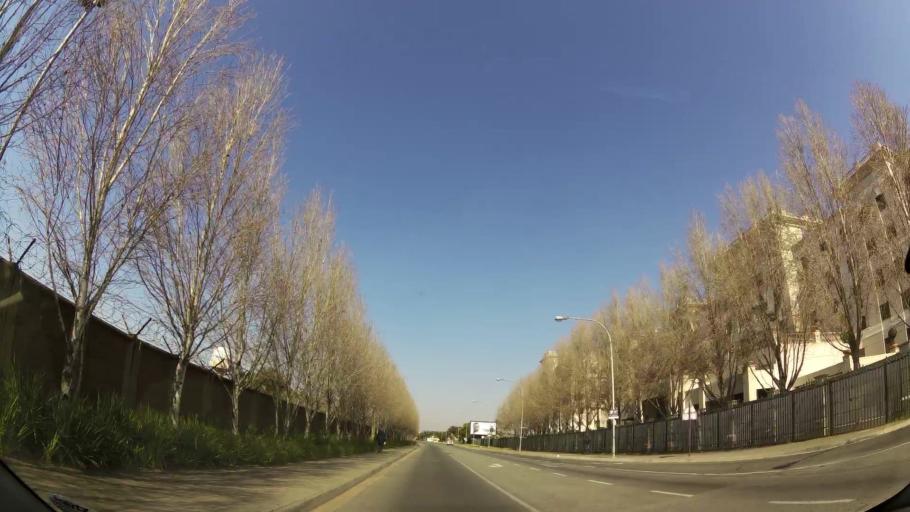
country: ZA
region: Gauteng
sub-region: Ekurhuleni Metropolitan Municipality
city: Boksburg
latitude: -26.1466
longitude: 28.2239
